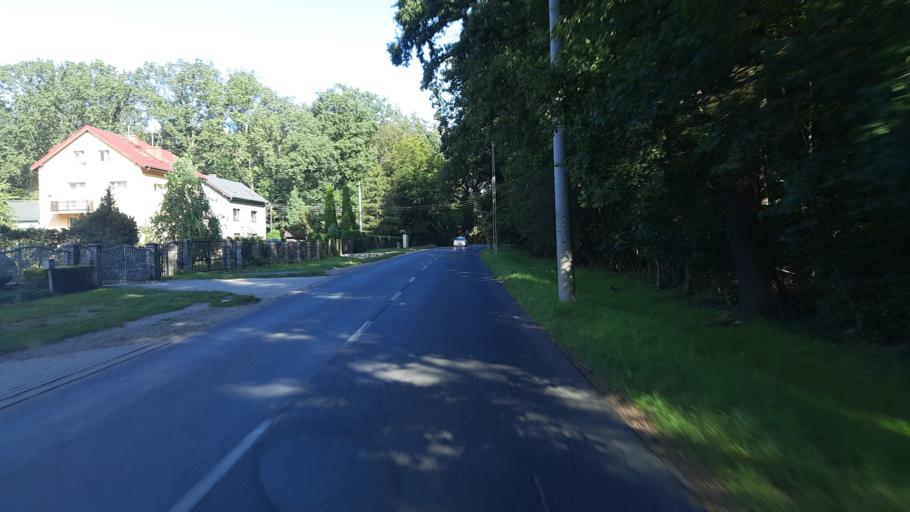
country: PL
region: Lower Silesian Voivodeship
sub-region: Powiat wroclawski
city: Dlugoleka
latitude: 51.1904
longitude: 17.1842
